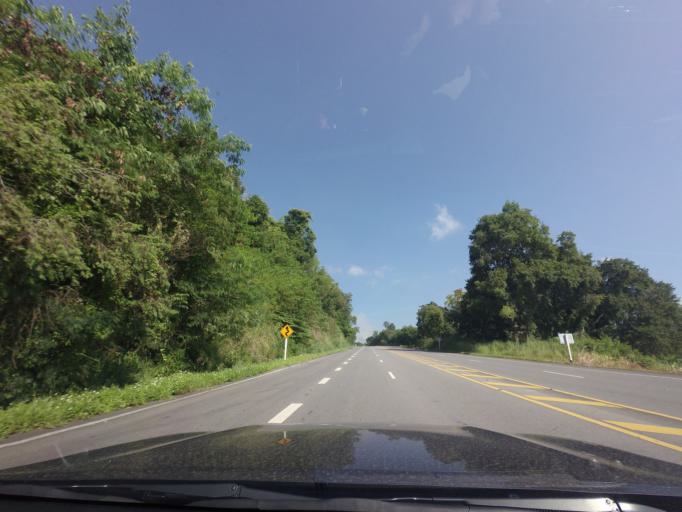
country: TH
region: Phetchabun
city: Khao Kho
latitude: 16.7812
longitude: 101.0919
